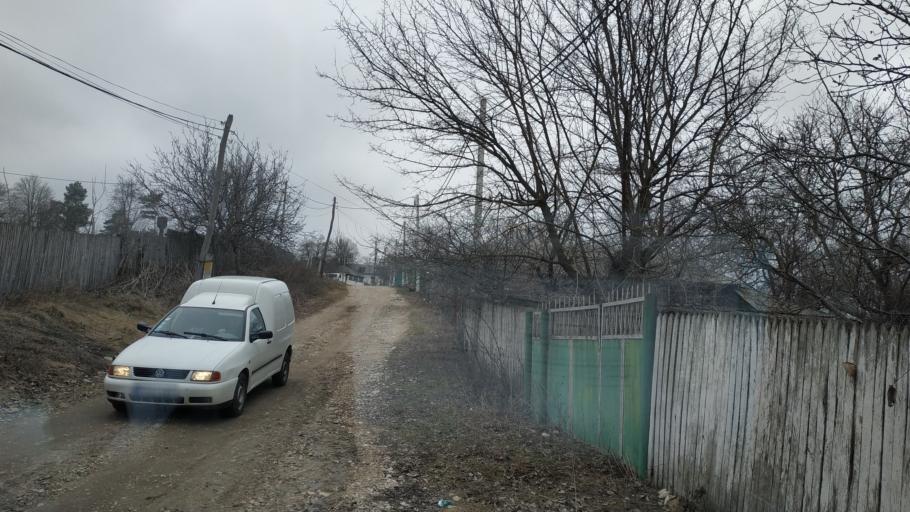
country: MD
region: Hincesti
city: Hincesti
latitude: 46.9799
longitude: 28.4741
